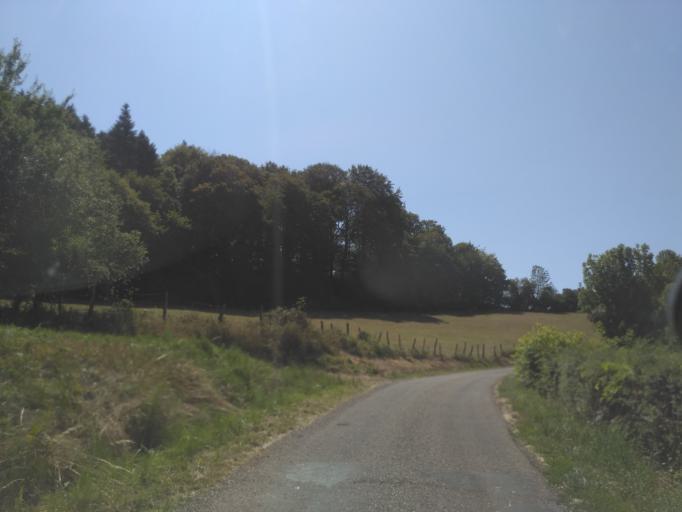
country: FR
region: Franche-Comte
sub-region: Departement de la Haute-Saone
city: Villersexel
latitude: 47.5019
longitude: 6.5291
